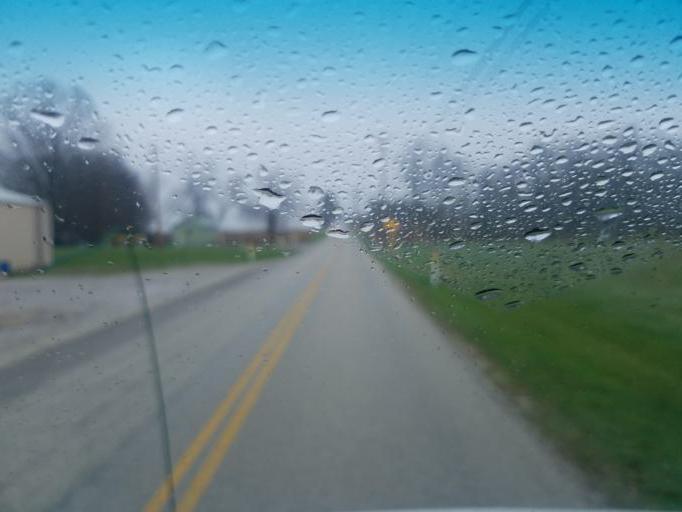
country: US
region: Ohio
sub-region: Wood County
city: North Baltimore
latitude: 41.1462
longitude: -83.6312
